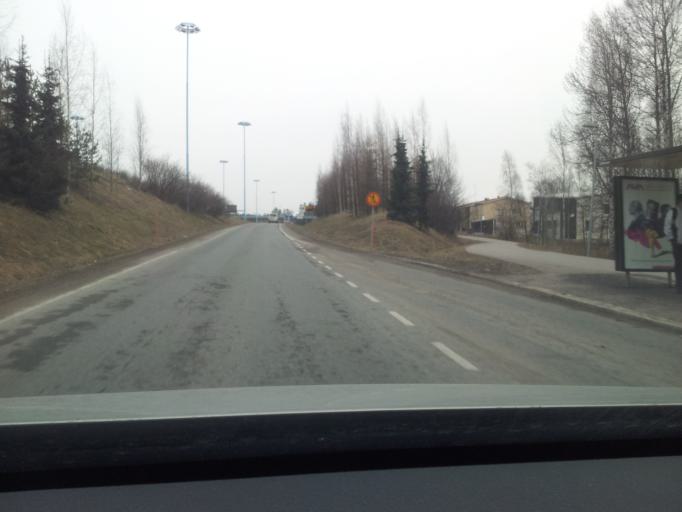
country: FI
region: Uusimaa
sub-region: Helsinki
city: Koukkuniemi
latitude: 60.1711
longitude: 24.7545
